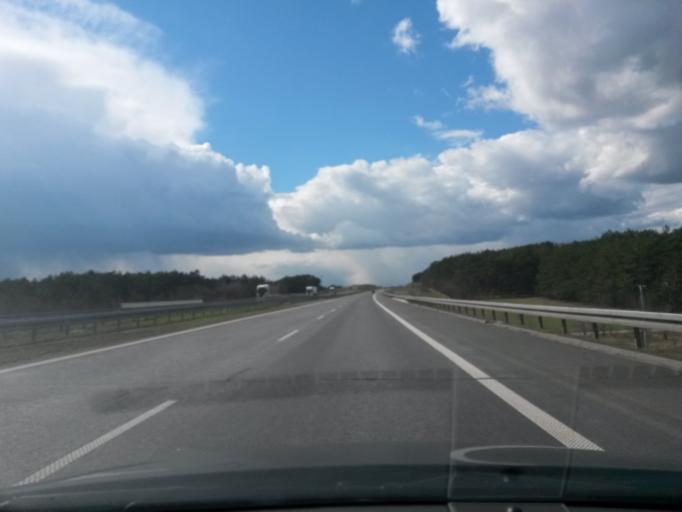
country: PL
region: Greater Poland Voivodeship
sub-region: Powiat kolski
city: Koscielec
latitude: 52.1421
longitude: 18.5344
